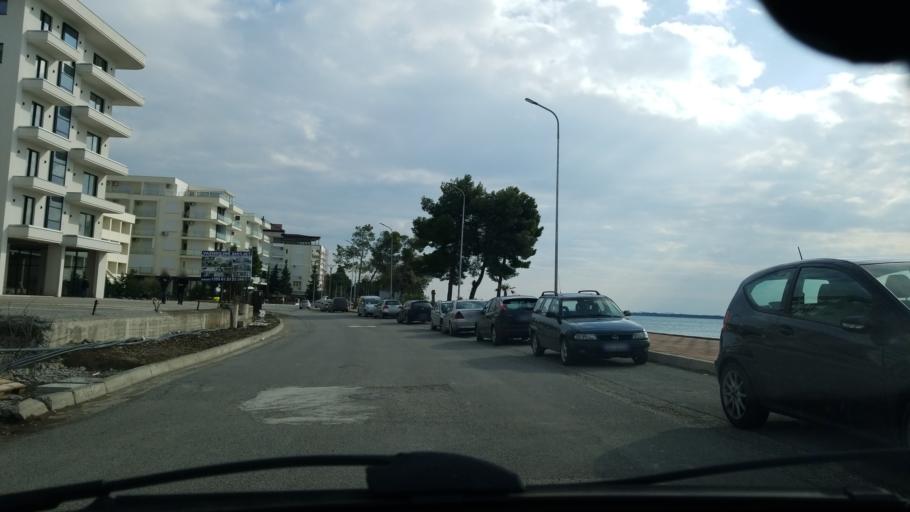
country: AL
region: Lezhe
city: Shengjin
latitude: 41.7978
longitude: 19.6015
